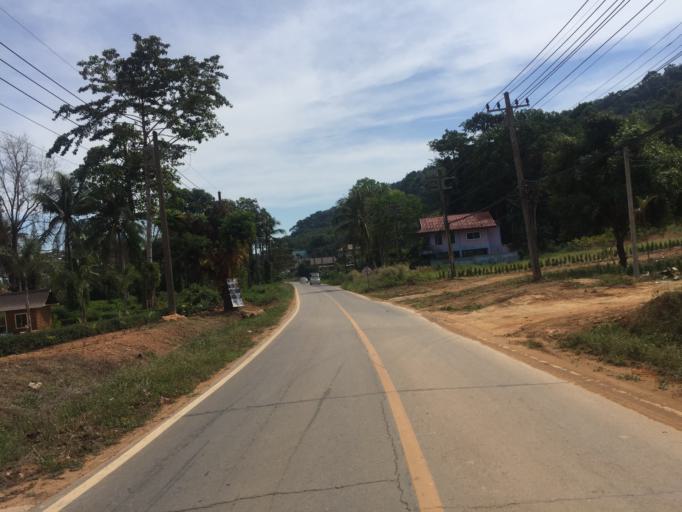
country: TH
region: Trat
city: Laem Ngop
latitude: 12.1175
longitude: 102.3384
